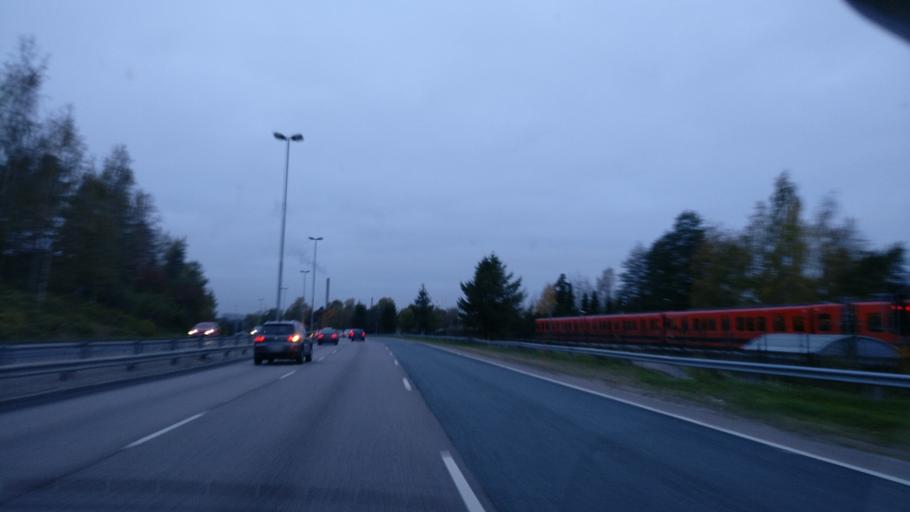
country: FI
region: Uusimaa
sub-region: Helsinki
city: Helsinki
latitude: 60.1886
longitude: 25.0075
